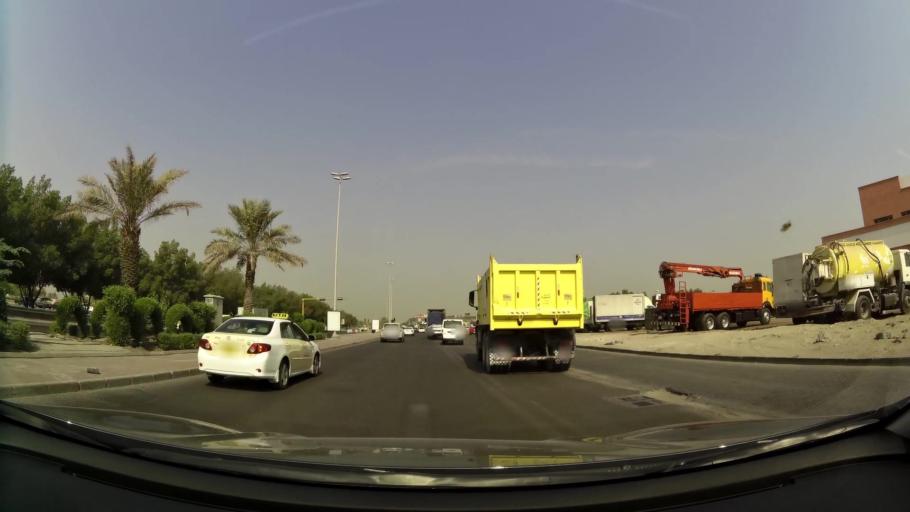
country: KW
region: Al Asimah
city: Ar Rabiyah
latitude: 29.3173
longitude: 47.9257
